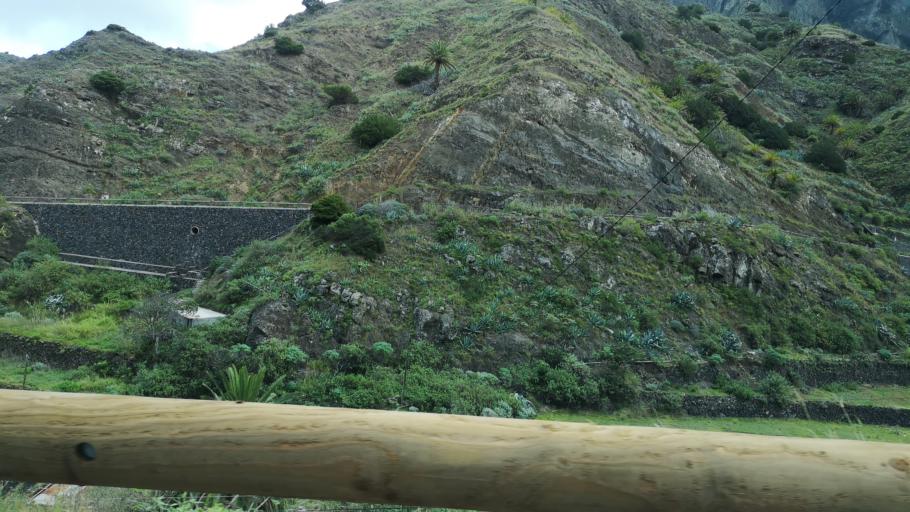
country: ES
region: Canary Islands
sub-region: Provincia de Santa Cruz de Tenerife
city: Hermigua
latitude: 28.1442
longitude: -17.1969
